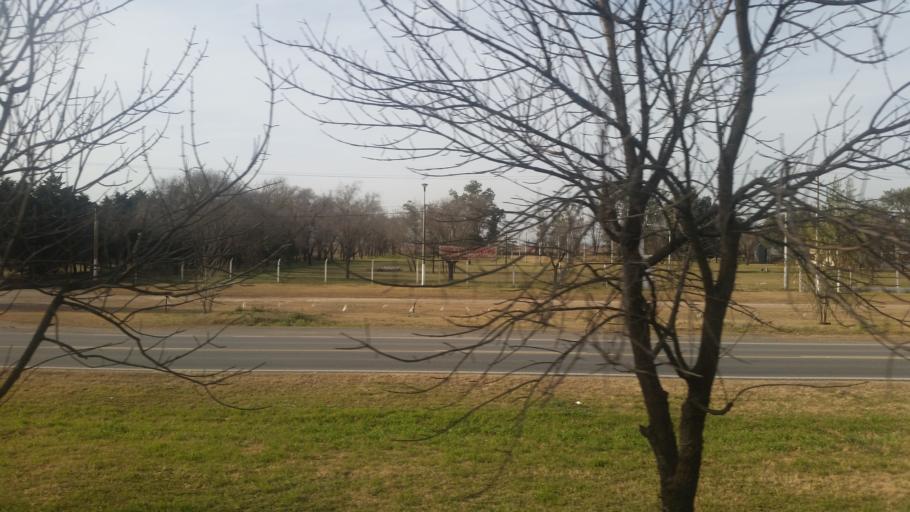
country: AR
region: Cordoba
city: Laguna Larga
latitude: -31.7704
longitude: -63.8088
